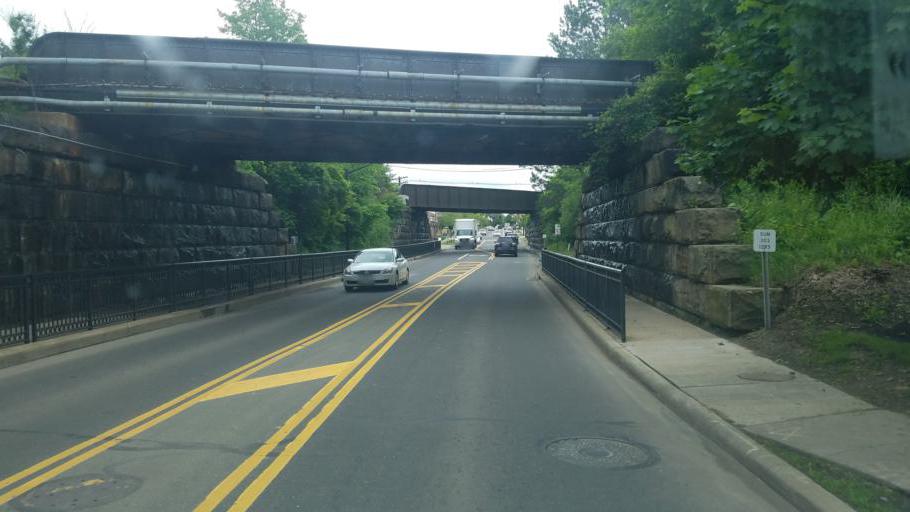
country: US
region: Ohio
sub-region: Summit County
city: Hudson
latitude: 41.2399
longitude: -81.4449
